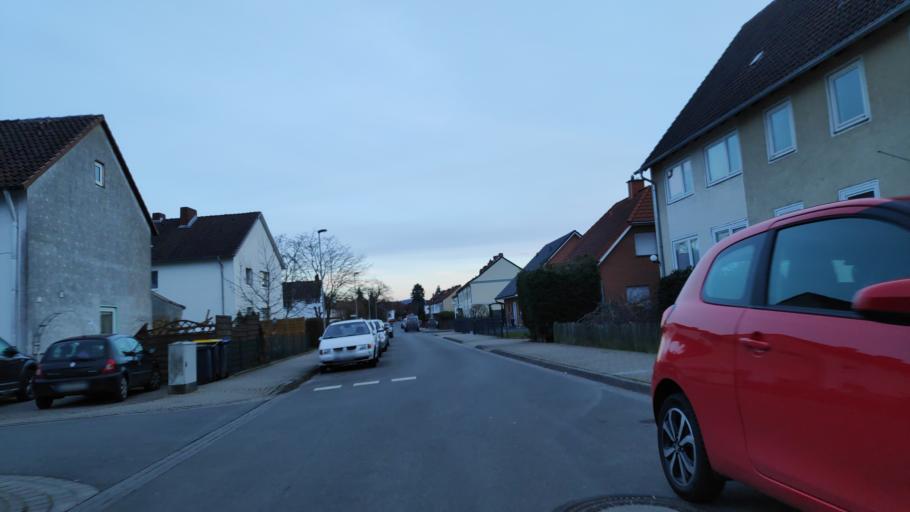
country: DE
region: North Rhine-Westphalia
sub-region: Regierungsbezirk Detmold
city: Minden
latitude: 52.2952
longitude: 8.9453
